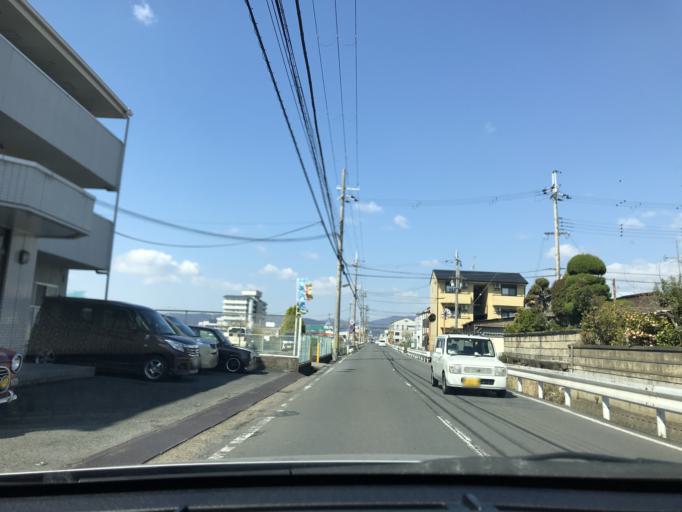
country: JP
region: Nara
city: Nara-shi
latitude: 34.6699
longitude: 135.8095
